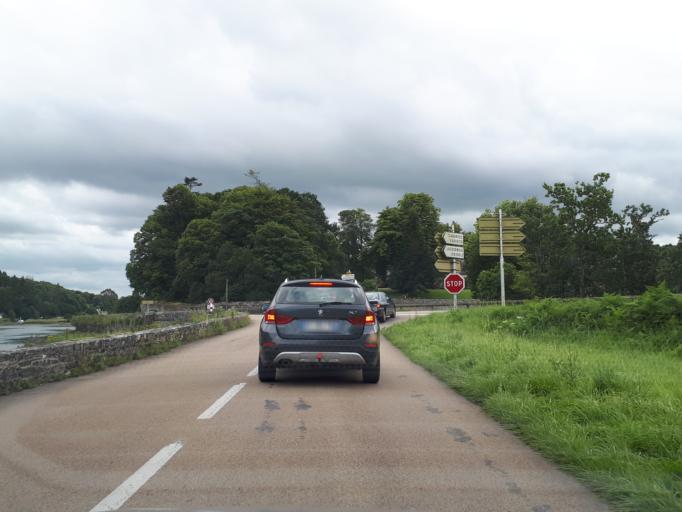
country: FR
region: Brittany
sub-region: Departement du Finistere
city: Morlaix
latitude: 48.6092
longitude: -3.8581
